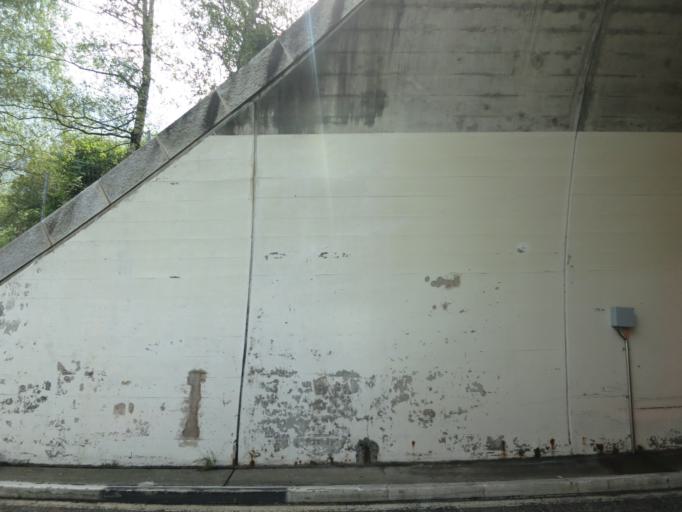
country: CH
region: Grisons
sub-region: Moesa District
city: Mesocco
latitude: 46.3888
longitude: 9.2336
